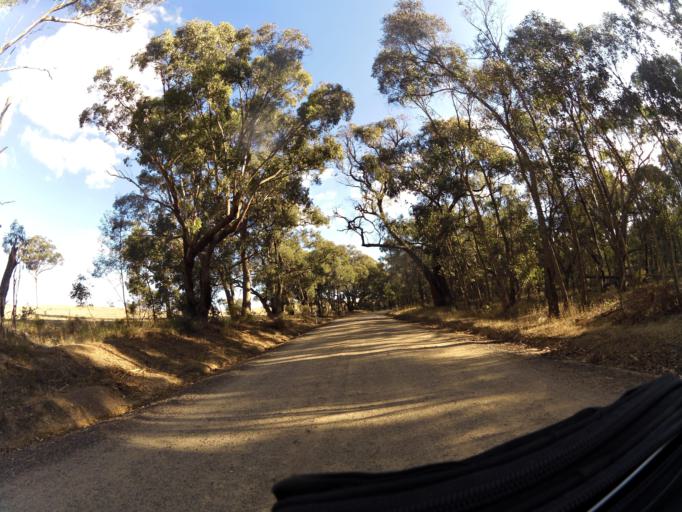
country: AU
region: Victoria
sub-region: Greater Bendigo
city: Kennington
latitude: -37.0195
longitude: 144.8049
